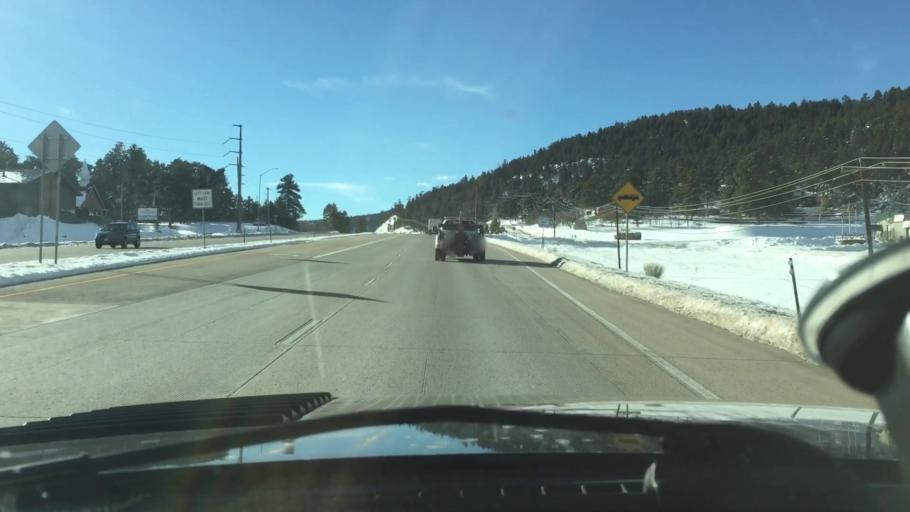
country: US
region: Colorado
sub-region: Jefferson County
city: Indian Hills
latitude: 39.5653
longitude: -105.2390
